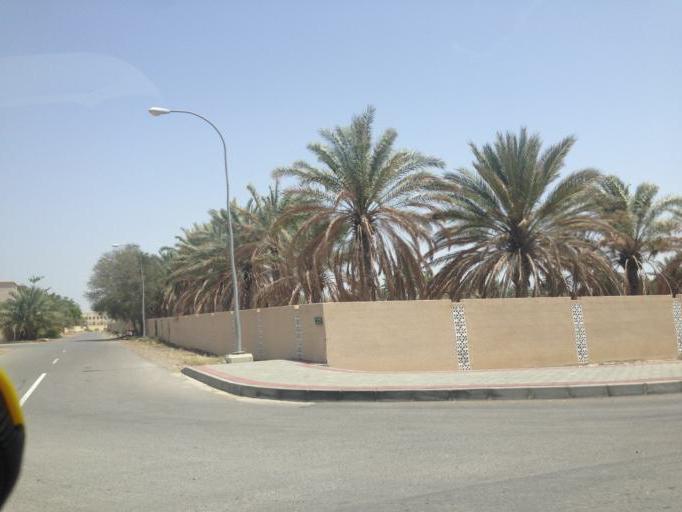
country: OM
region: Muhafazat Masqat
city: As Sib al Jadidah
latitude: 23.6879
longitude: 58.1049
